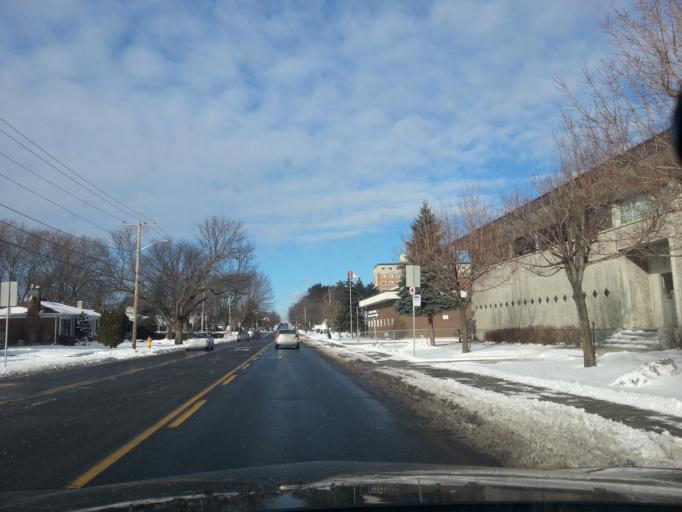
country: CA
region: Ontario
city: Cornwall
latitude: 45.0238
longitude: -74.7142
